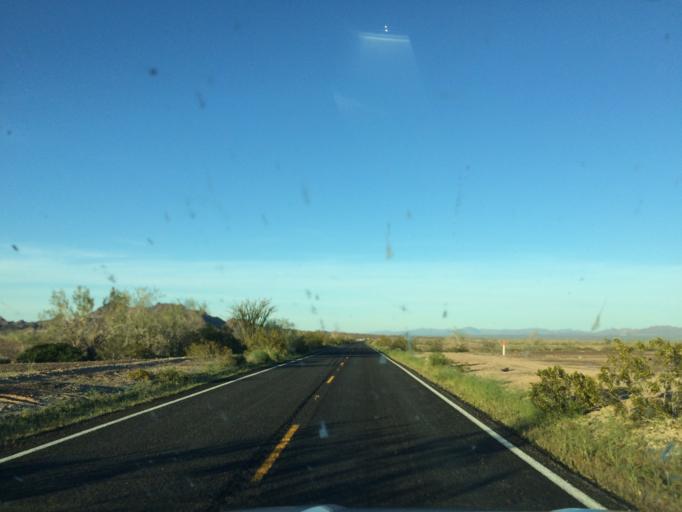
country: US
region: California
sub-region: Riverside County
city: Mesa Verde
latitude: 33.2641
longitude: -114.8026
